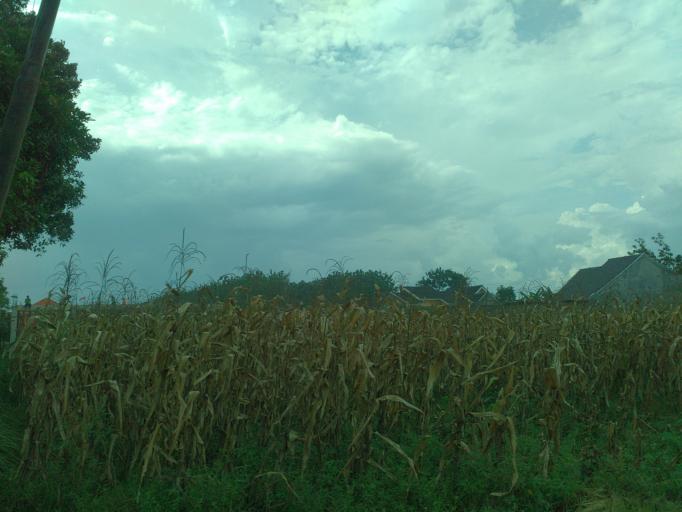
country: ID
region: Central Java
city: Ceper
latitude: -7.6755
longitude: 110.6529
